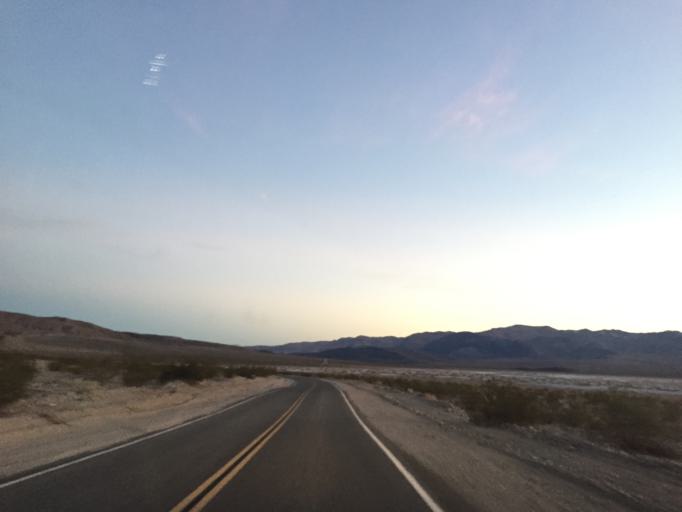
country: US
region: California
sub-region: San Bernardino County
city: Searles Valley
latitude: 35.9846
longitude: -116.7344
